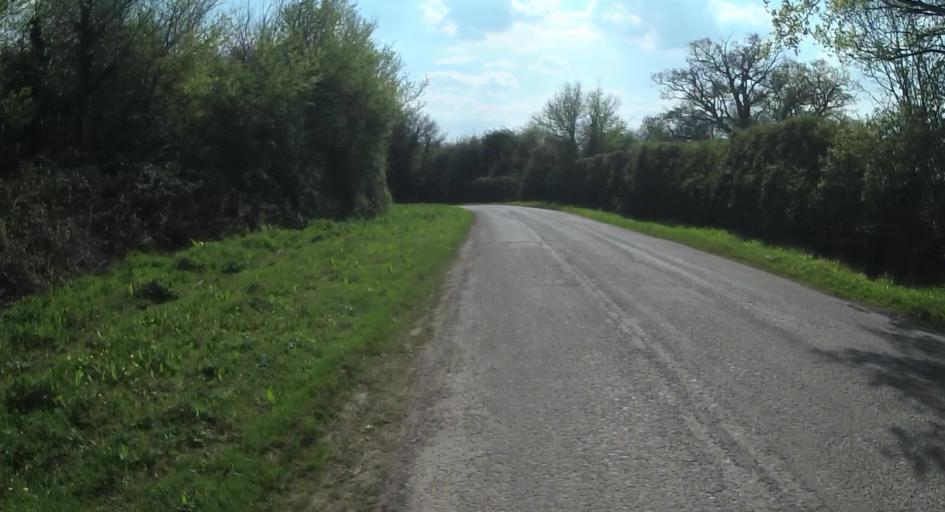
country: GB
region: England
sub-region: West Berkshire
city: Stratfield Mortimer
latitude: 51.3606
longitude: -1.0073
